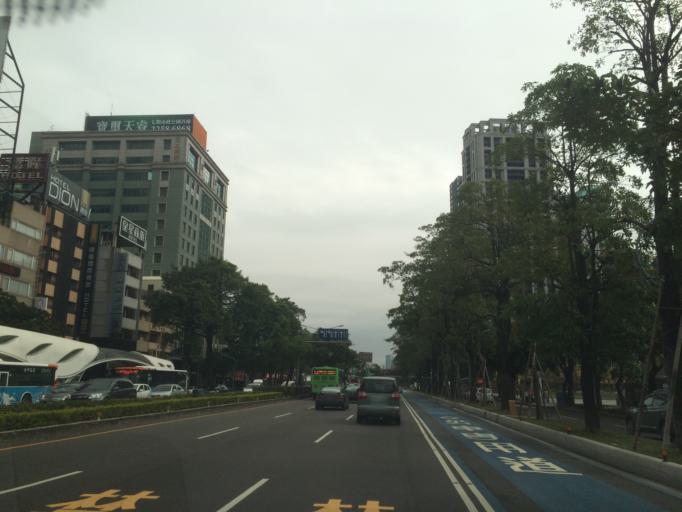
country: TW
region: Taiwan
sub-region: Taichung City
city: Taichung
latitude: 24.1689
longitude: 120.6393
